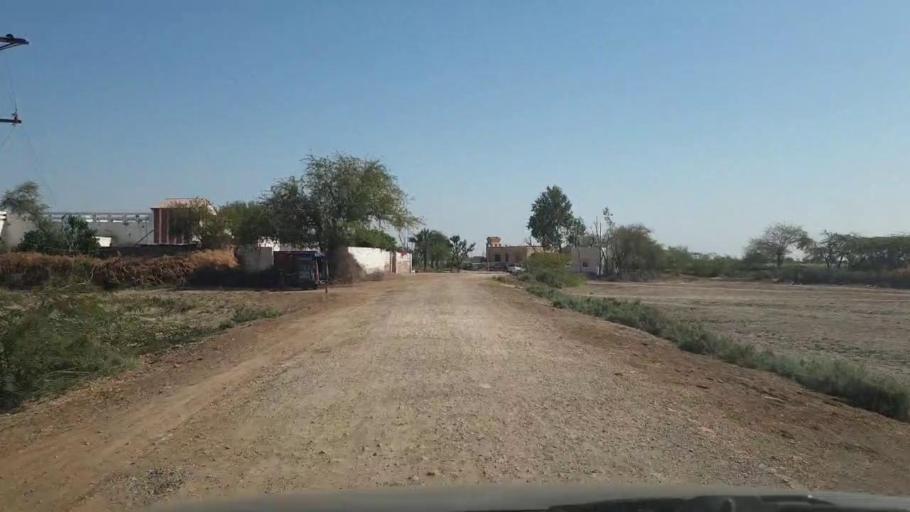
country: PK
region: Sindh
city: Dhoro Naro
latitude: 25.3844
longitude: 69.5986
